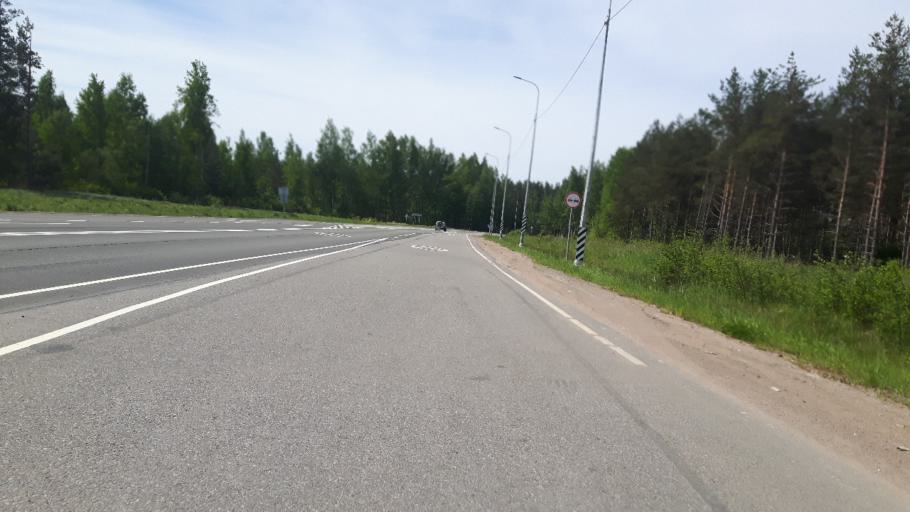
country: RU
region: Leningrad
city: Ust'-Luga
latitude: 59.6513
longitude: 28.3681
